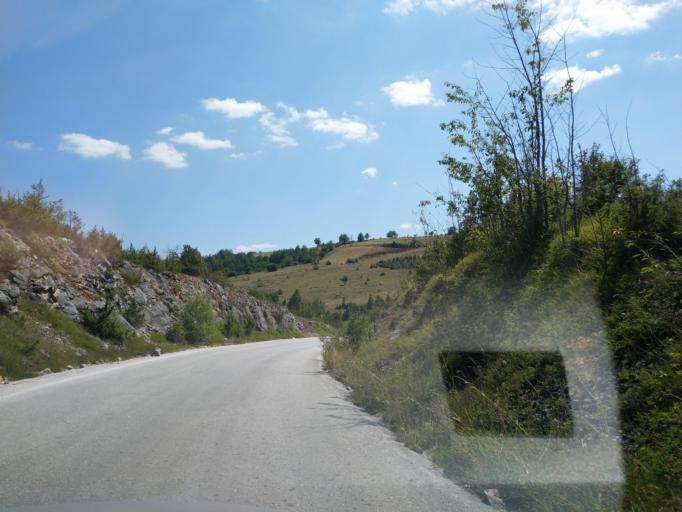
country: RS
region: Central Serbia
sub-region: Zlatiborski Okrug
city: Nova Varos
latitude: 43.4374
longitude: 19.9592
